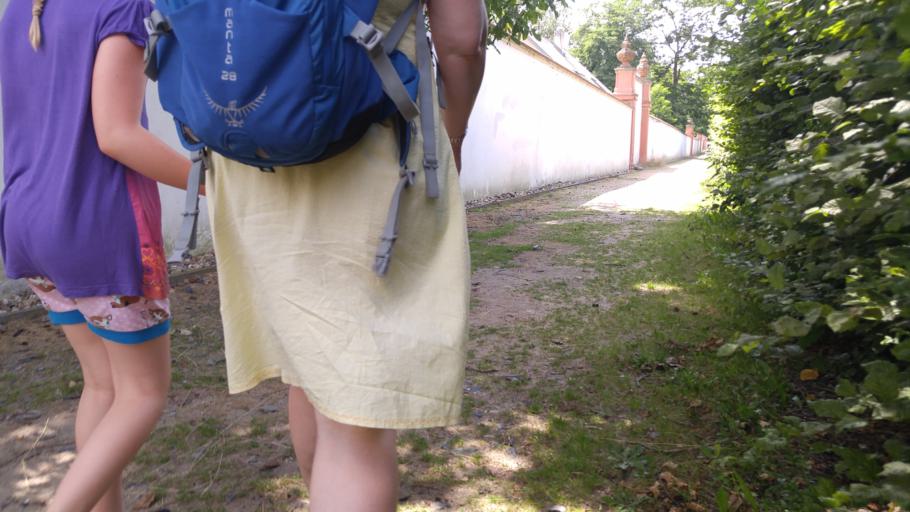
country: CZ
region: Praha
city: Prague
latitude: 50.1155
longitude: 14.4162
